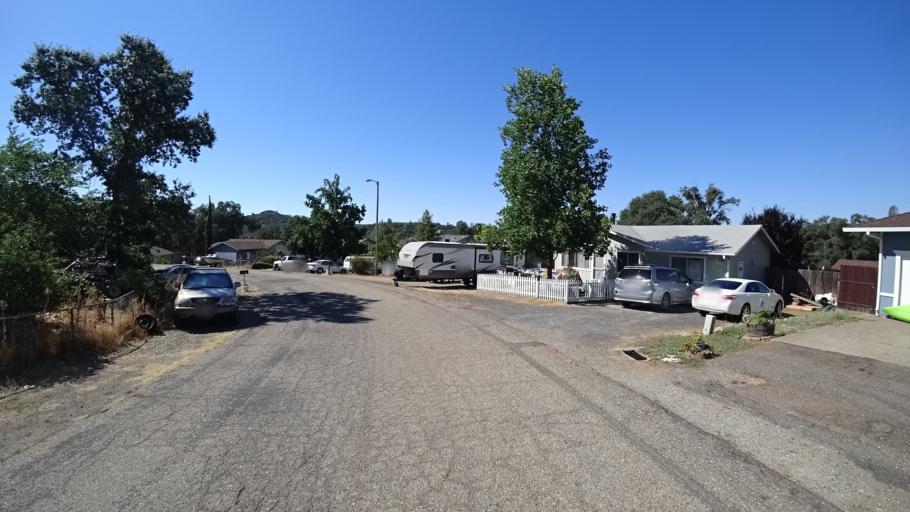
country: US
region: California
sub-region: Calaveras County
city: Murphys
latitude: 38.1094
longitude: -120.4596
